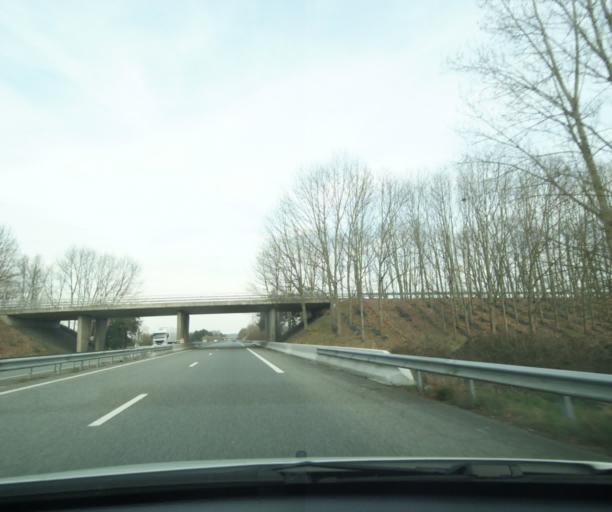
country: FR
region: Midi-Pyrenees
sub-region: Departement des Hautes-Pyrenees
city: Odos
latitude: 43.2098
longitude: 0.0582
